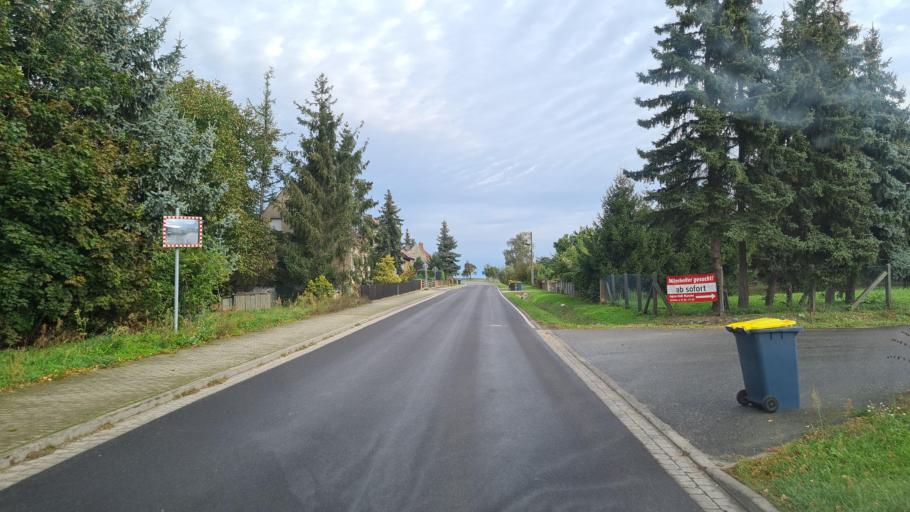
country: DE
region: Brandenburg
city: Luckau
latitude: 51.8717
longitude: 13.7235
